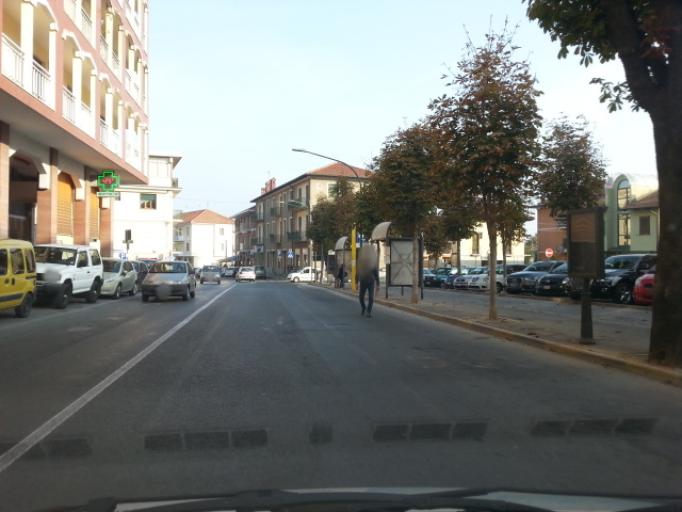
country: IT
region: Piedmont
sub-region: Provincia di Torino
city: Giaveno
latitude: 45.0407
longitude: 7.3542
